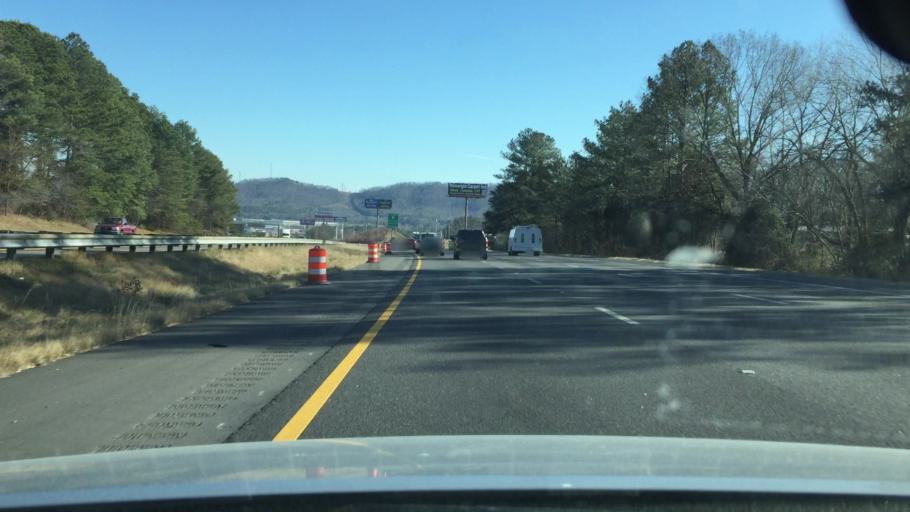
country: US
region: Georgia
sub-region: Catoosa County
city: Ringgold
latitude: 34.9136
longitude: -85.1413
